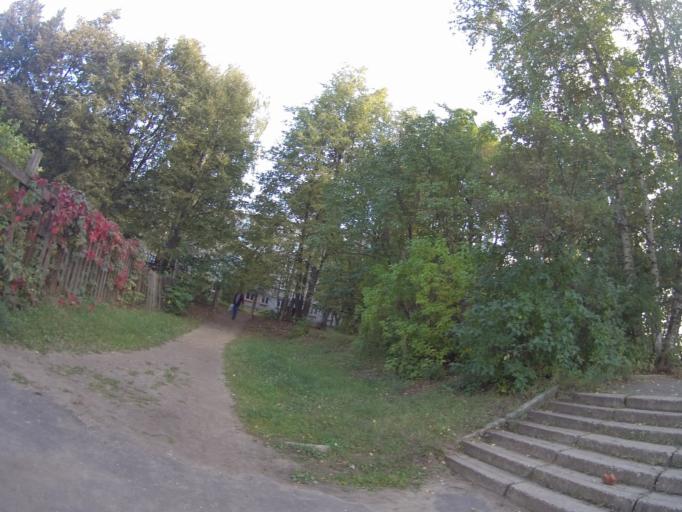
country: RU
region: Vladimir
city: Vladimir
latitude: 56.1116
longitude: 40.3398
